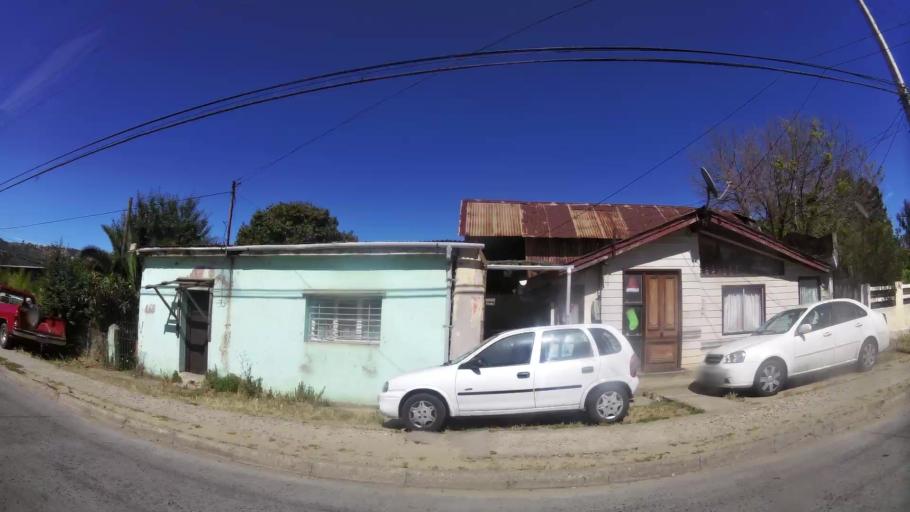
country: CL
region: Valparaiso
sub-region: Provincia de Valparaiso
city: Valparaiso
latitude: -33.0619
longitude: -71.5864
